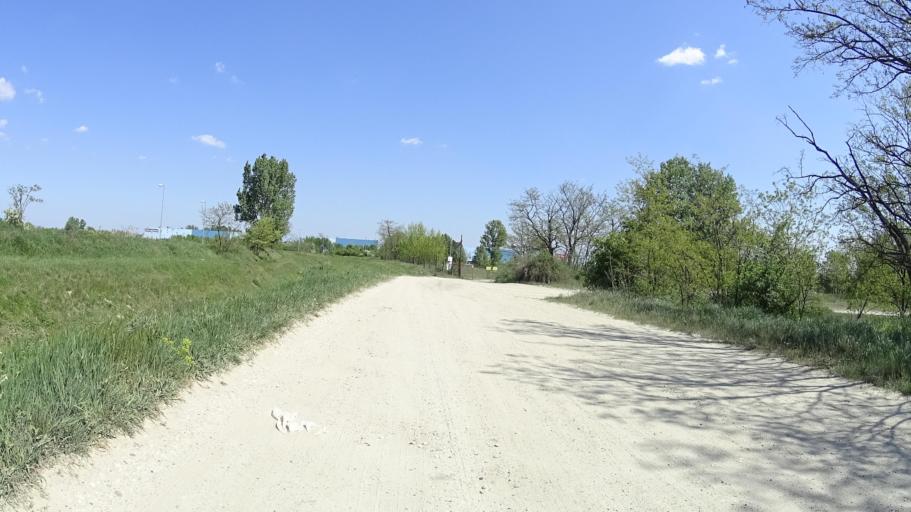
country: HU
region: Pest
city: Gyal
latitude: 47.3654
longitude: 19.2111
